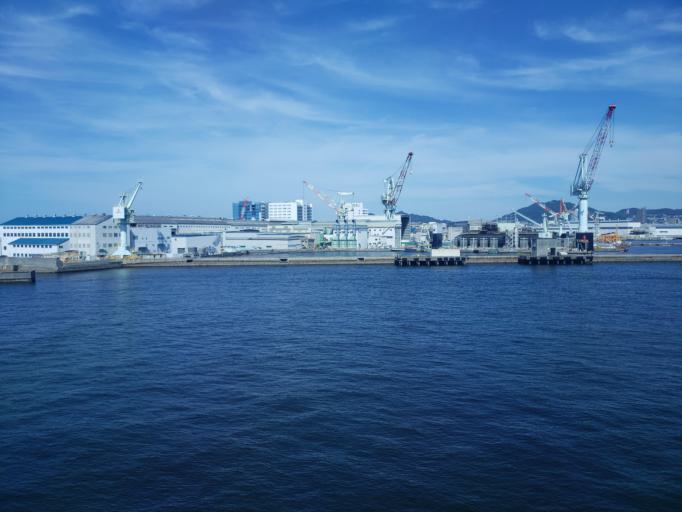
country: JP
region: Hyogo
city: Kobe
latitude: 34.6540
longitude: 135.1886
